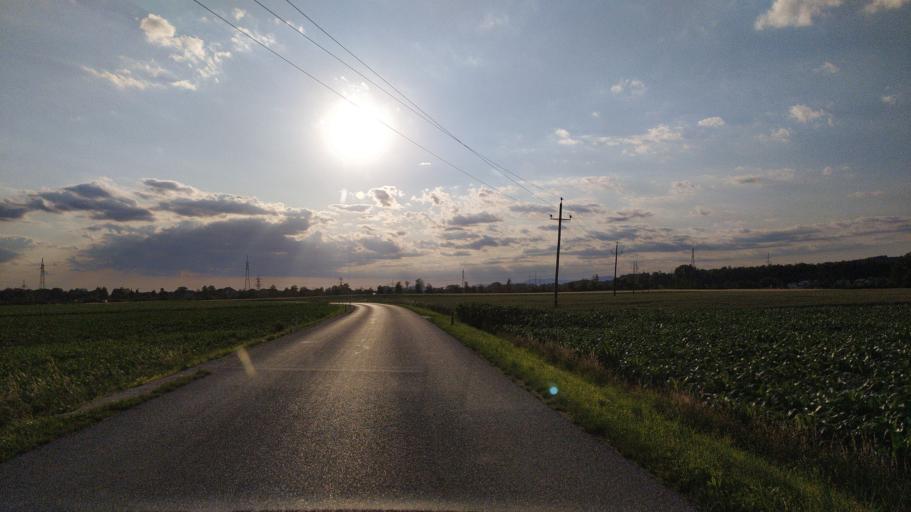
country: AT
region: Lower Austria
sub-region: Politischer Bezirk Amstetten
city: Ennsdorf
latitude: 48.2259
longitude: 14.5406
